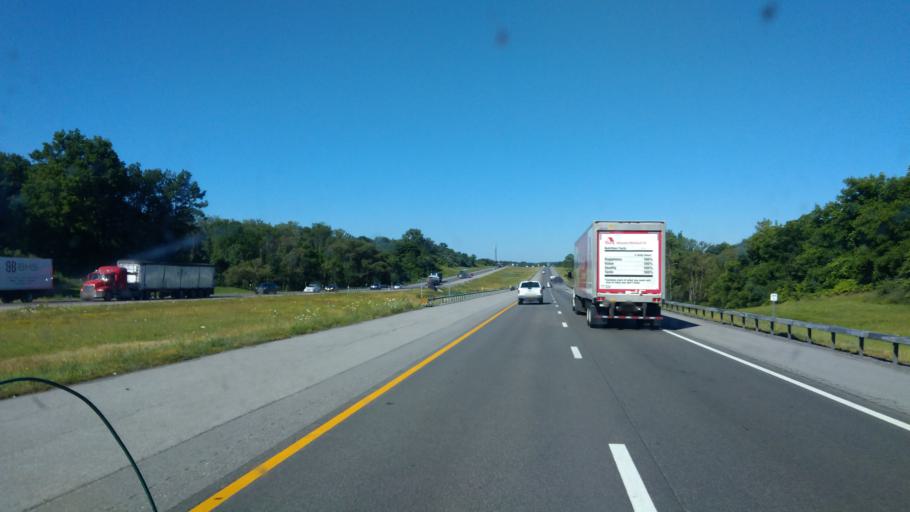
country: US
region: New York
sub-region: Genesee County
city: Le Roy
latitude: 43.0192
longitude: -78.0788
